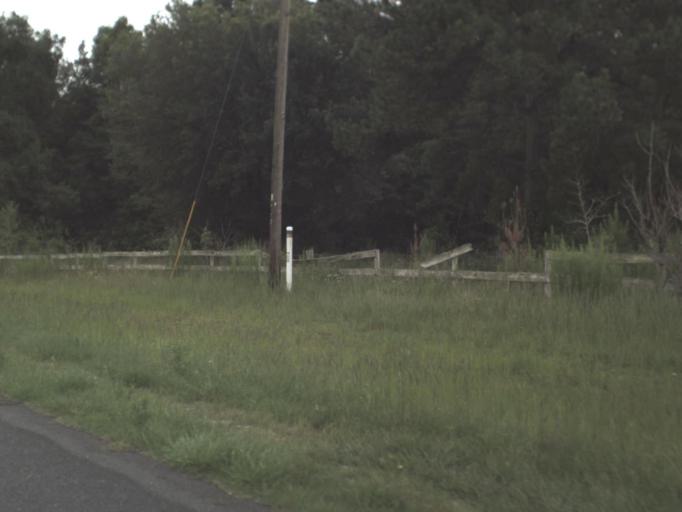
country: US
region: Florida
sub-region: Levy County
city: Williston
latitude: 29.2943
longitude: -82.4474
